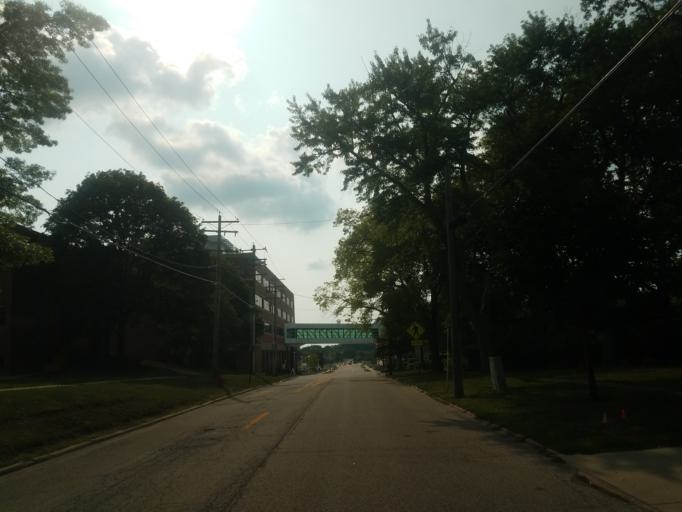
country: US
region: Illinois
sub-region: McLean County
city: Bloomington
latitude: 40.4982
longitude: -88.9897
